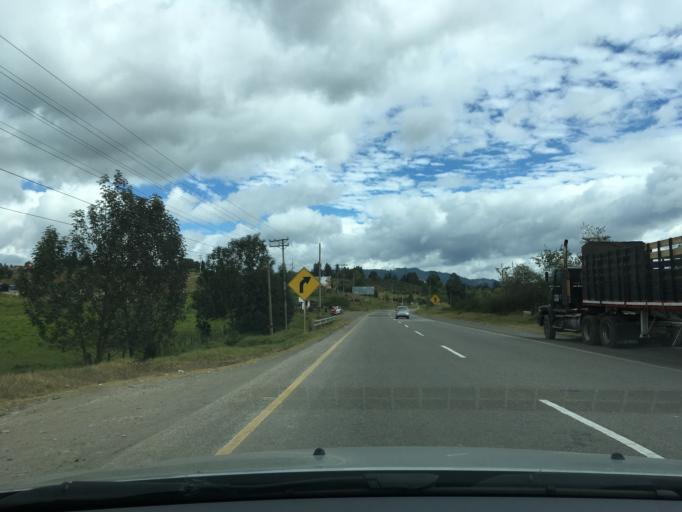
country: CO
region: Boyaca
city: Tuta
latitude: 5.7262
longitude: -73.2225
